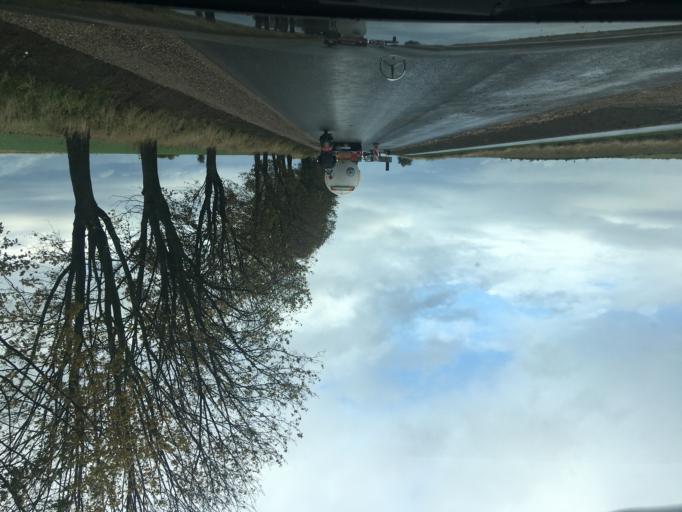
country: PL
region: Lublin Voivodeship
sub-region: Powiat lubelski
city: Wysokie
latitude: 50.9414
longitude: 22.6746
